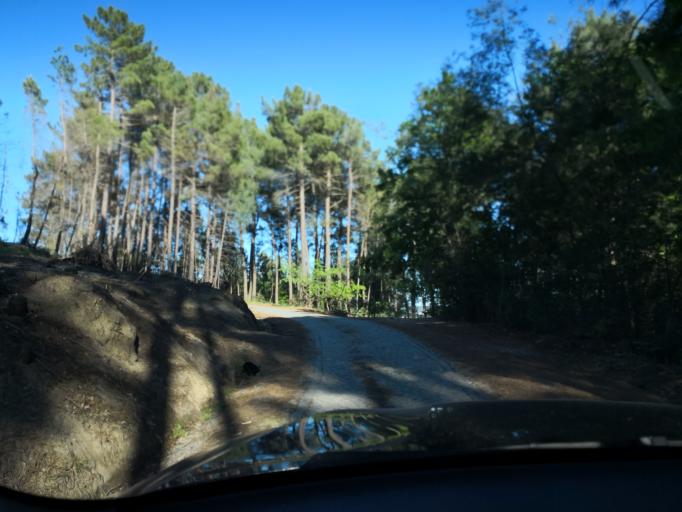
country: PT
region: Vila Real
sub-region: Vila Real
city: Vila Real
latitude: 41.3353
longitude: -7.7534
